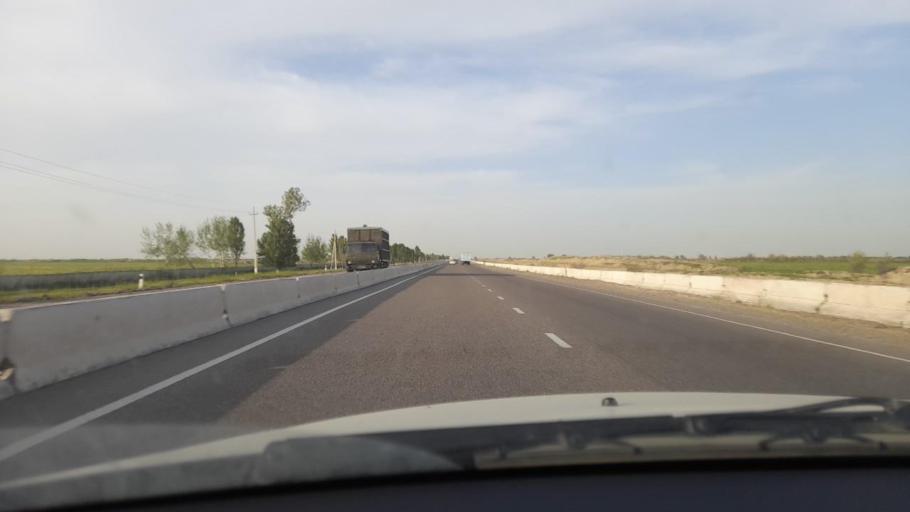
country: UZ
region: Jizzax
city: Dustlik
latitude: 40.4273
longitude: 68.2213
